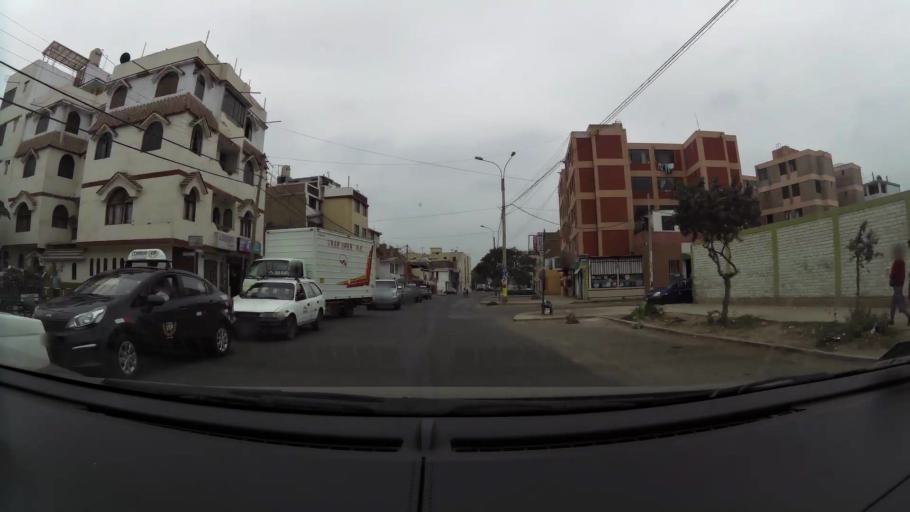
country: PE
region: La Libertad
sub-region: Provincia de Trujillo
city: Trujillo
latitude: -8.1233
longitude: -79.0312
